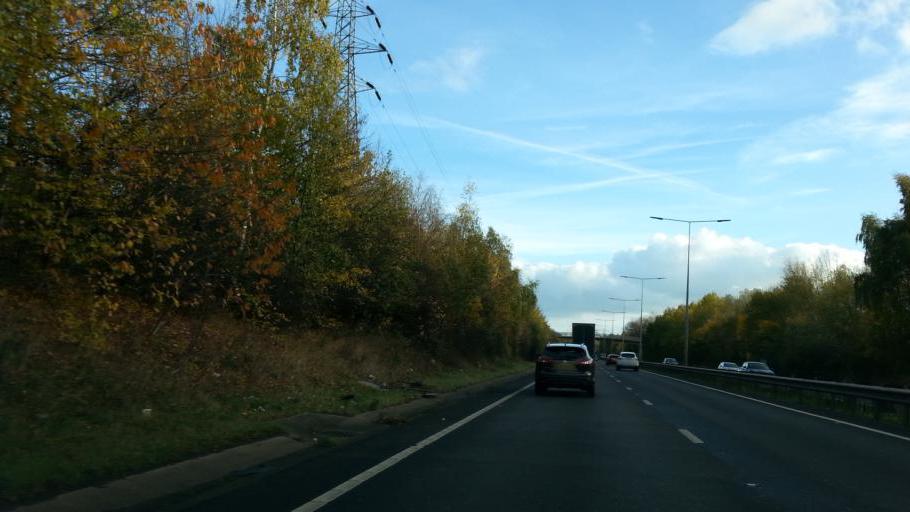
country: GB
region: England
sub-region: Staffordshire
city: Fazeley
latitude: 52.6163
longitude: -1.6654
